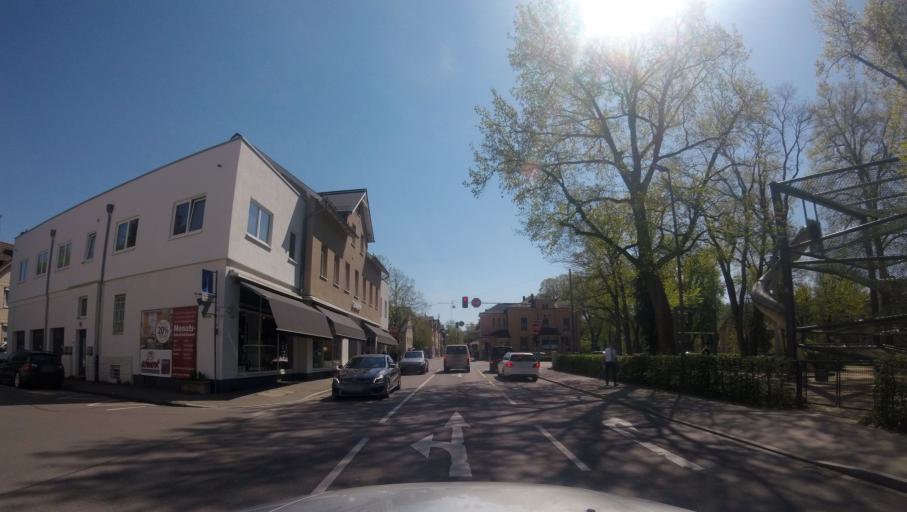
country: DE
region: Baden-Wuerttemberg
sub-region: Regierungsbezirk Stuttgart
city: Schwabisch Gmund
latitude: 48.7972
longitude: 9.7942
